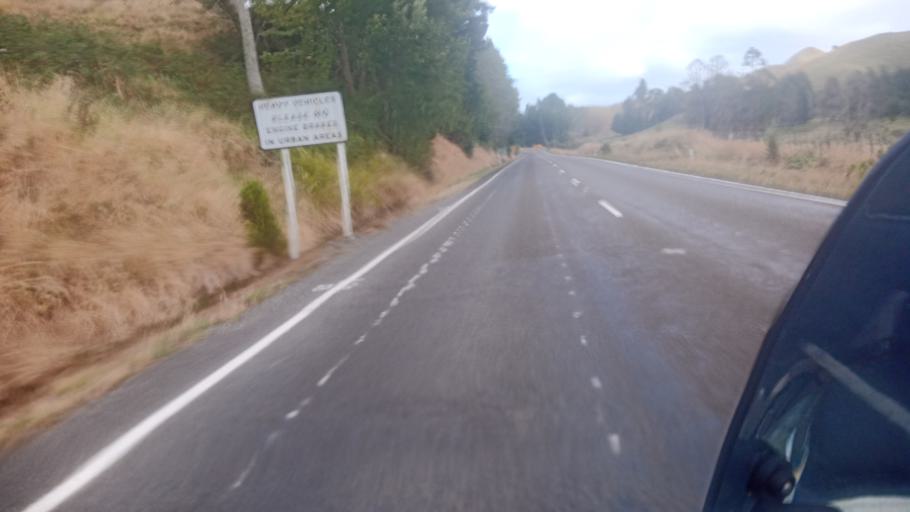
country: NZ
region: Bay of Plenty
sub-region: Opotiki District
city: Opotiki
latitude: -38.3611
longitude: 177.5426
